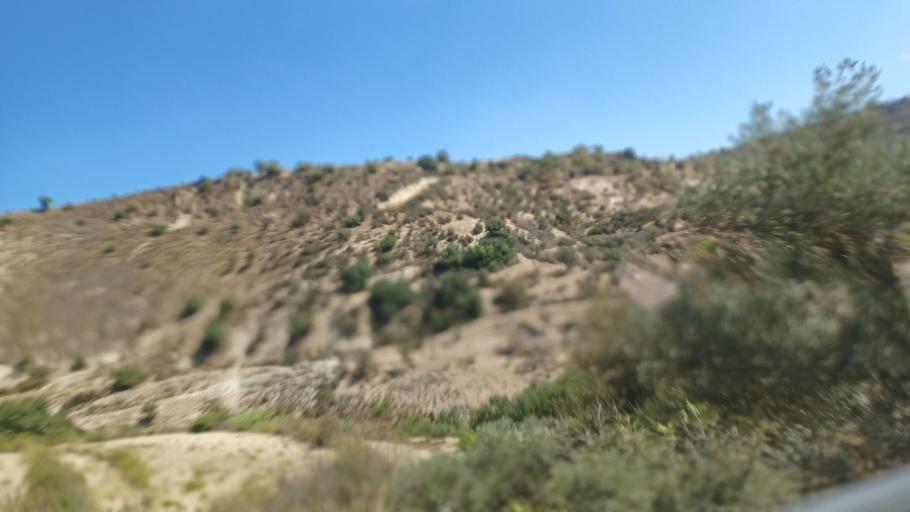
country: CY
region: Pafos
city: Mesogi
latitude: 34.8432
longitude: 32.5127
